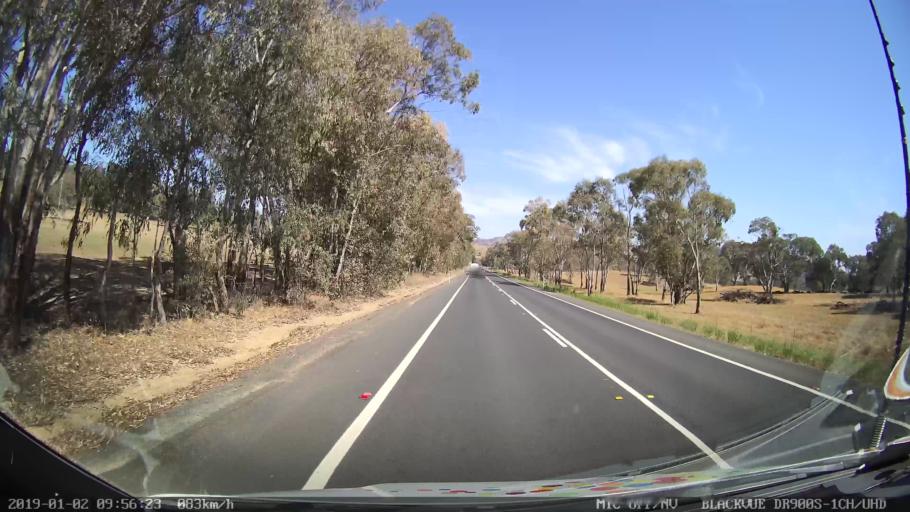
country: AU
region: New South Wales
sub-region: Tumut Shire
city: Tumut
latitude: -35.2156
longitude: 148.1772
